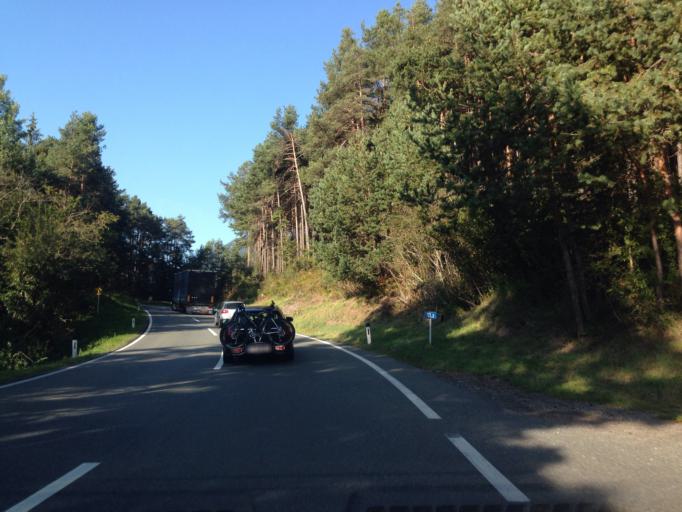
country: AT
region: Tyrol
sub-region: Politischer Bezirk Imst
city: Obsteig
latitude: 47.2991
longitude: 10.9455
